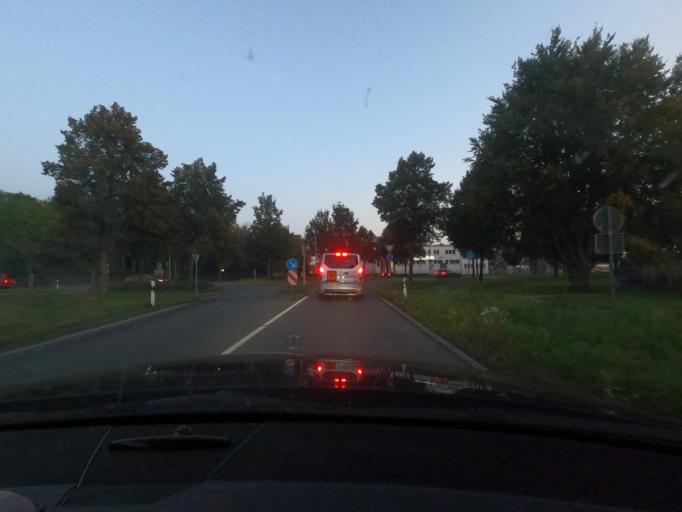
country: DE
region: North Rhine-Westphalia
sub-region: Regierungsbezirk Detmold
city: Salzkotten
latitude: 51.6655
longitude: 8.5890
